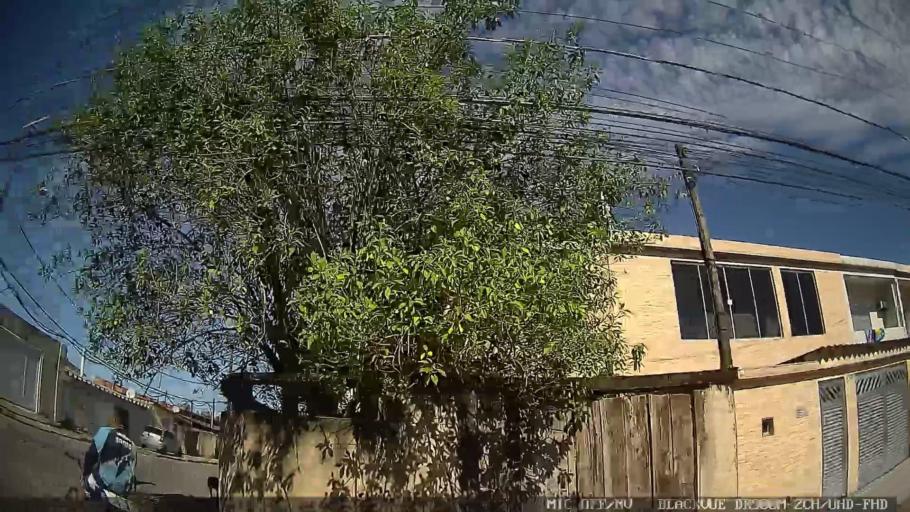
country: BR
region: Sao Paulo
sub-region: Guaruja
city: Guaruja
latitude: -23.9531
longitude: -46.2788
